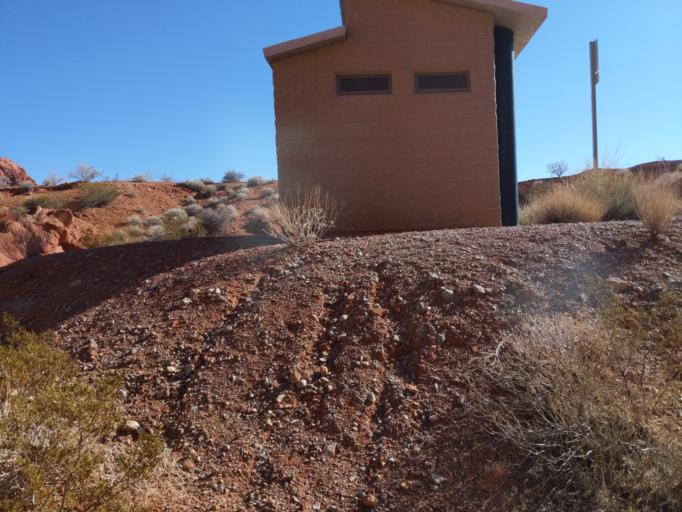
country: US
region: Nevada
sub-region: Clark County
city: Moapa Valley
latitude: 36.4301
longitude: -114.4815
